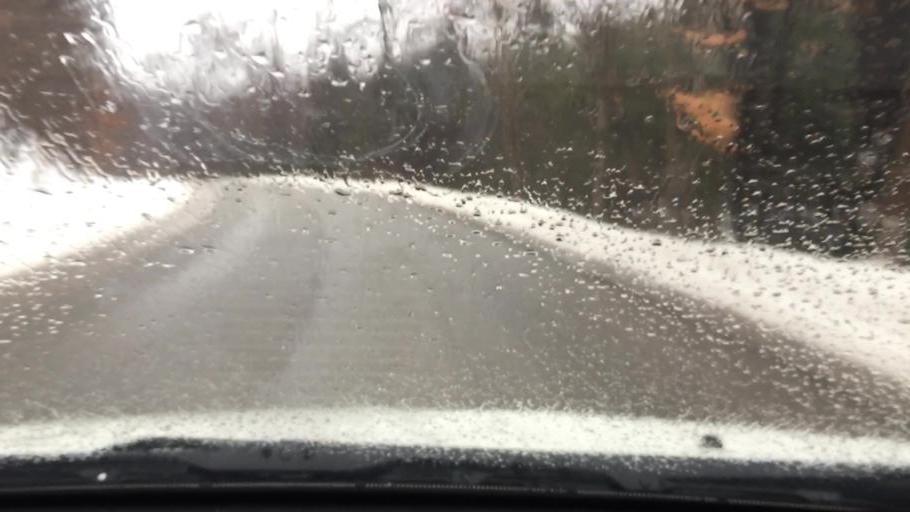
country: US
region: Michigan
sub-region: Charlevoix County
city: East Jordan
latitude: 45.1036
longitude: -85.1448
